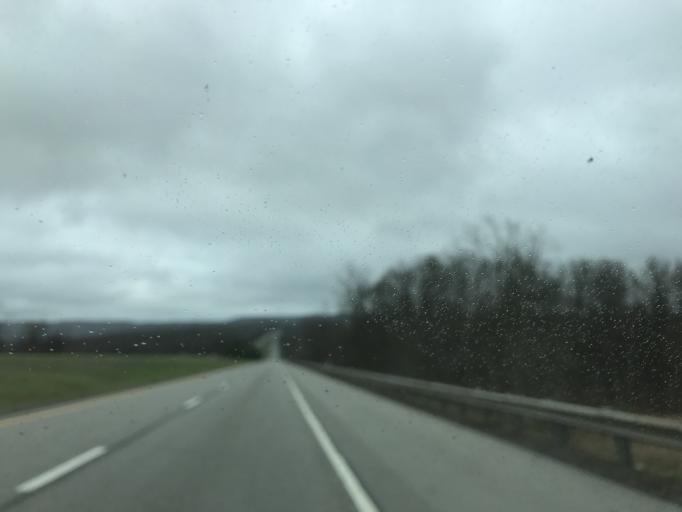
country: US
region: West Virginia
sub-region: Greenbrier County
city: Lewisburg
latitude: 37.8967
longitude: -80.5877
